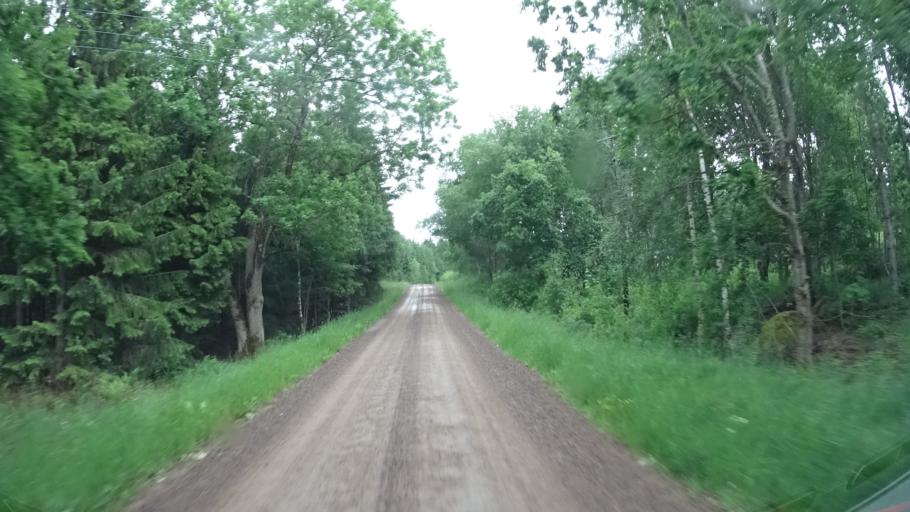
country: SE
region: Joenkoeping
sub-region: Eksjo Kommun
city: Mariannelund
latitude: 57.6193
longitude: 15.6583
